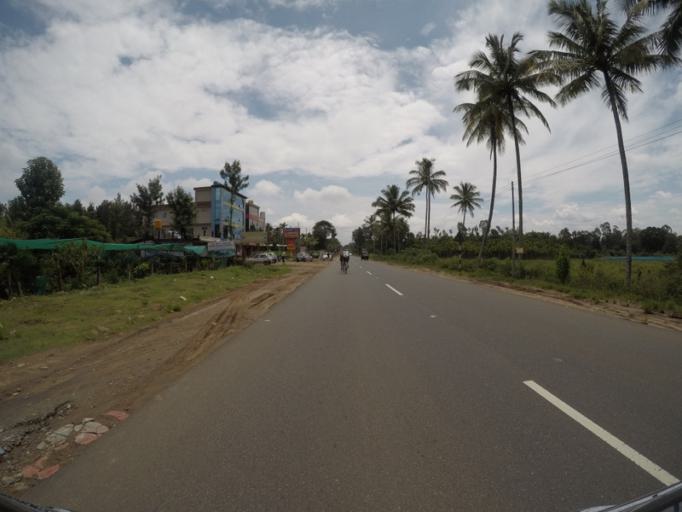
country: IN
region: Karnataka
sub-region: Kodagu
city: Kushalnagar
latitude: 12.4453
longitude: 75.9269
